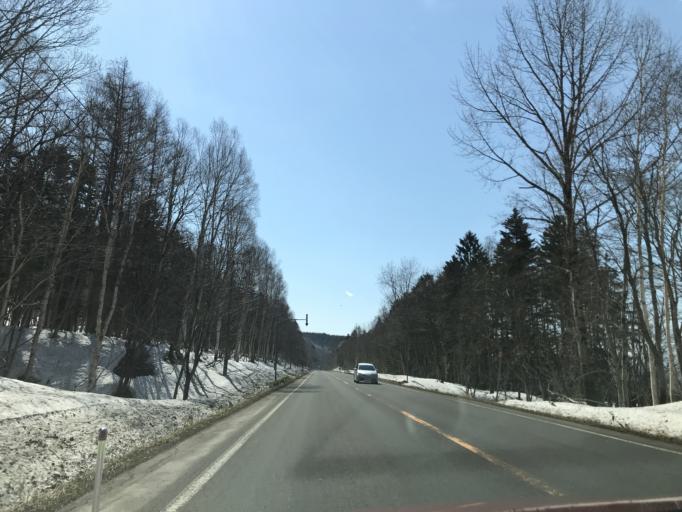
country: JP
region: Hokkaido
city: Nayoro
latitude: 44.7162
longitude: 142.2723
